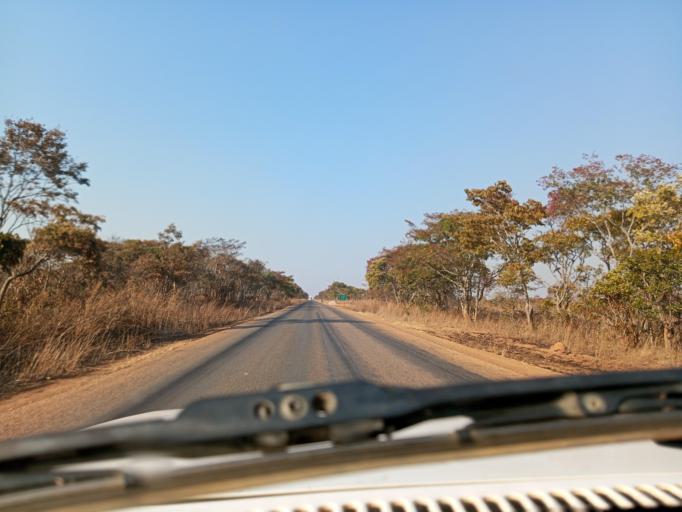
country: ZM
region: Northern
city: Mpika
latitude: -12.4053
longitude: 31.0866
